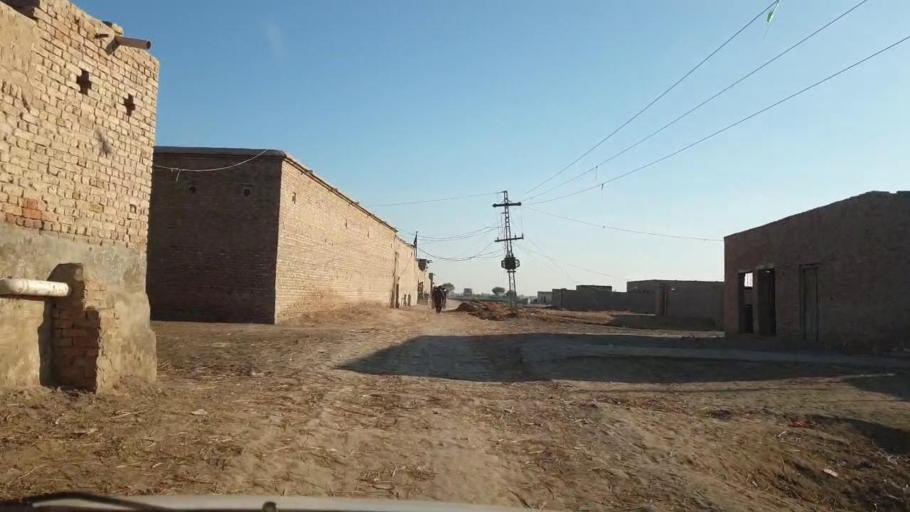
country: PK
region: Sindh
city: Khairpur Nathan Shah
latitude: 27.0486
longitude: 67.7242
